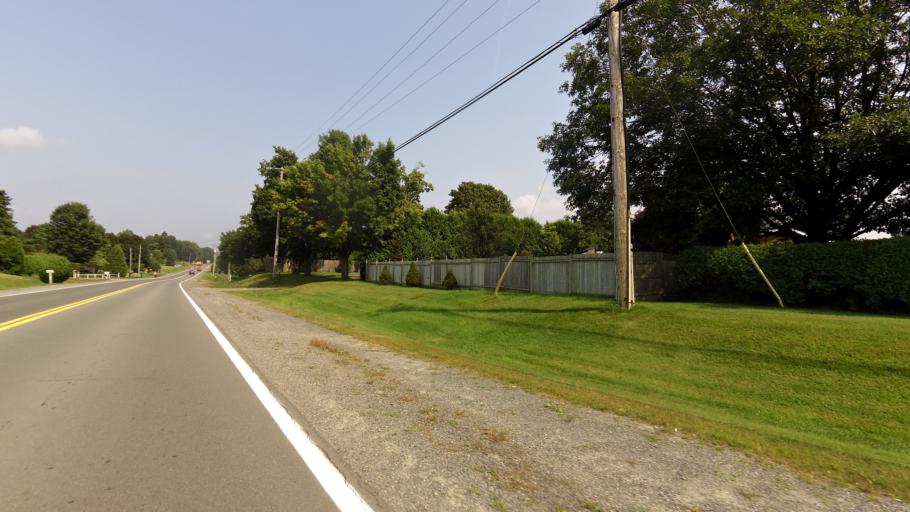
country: CA
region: Ontario
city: Prescott
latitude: 44.6848
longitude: -75.5544
